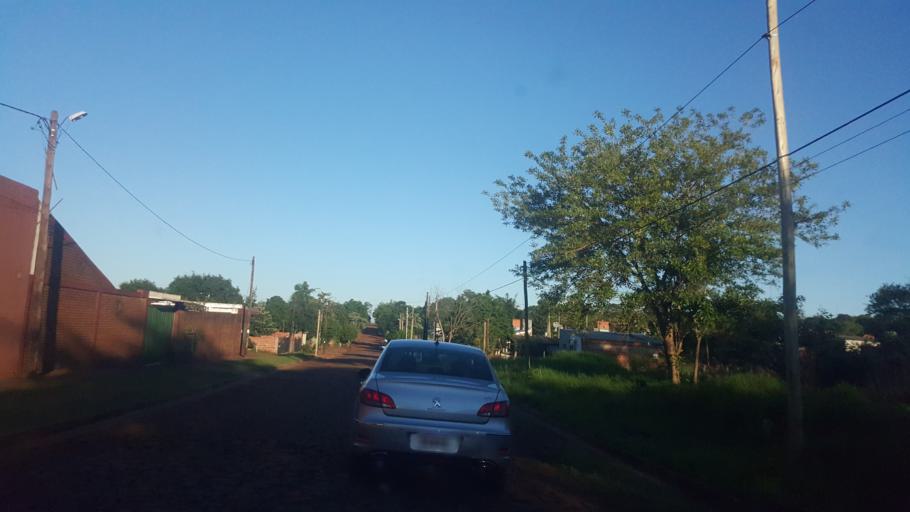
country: AR
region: Misiones
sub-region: Departamento de Capital
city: Posadas
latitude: -27.4228
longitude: -55.9253
